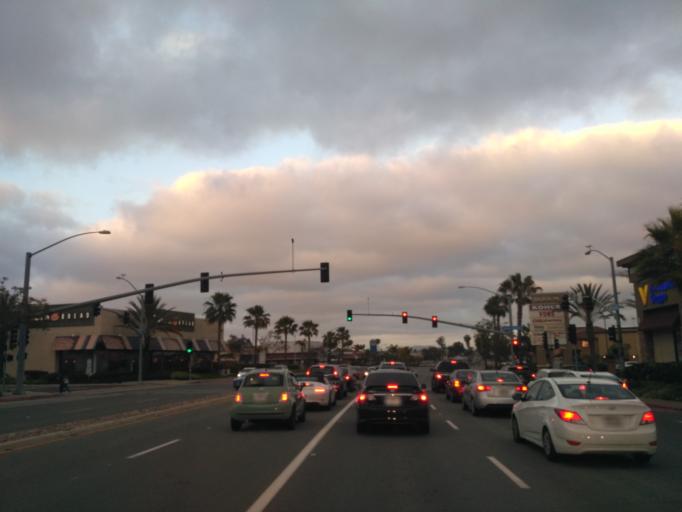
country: US
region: California
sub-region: San Diego County
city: La Jolla
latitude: 32.8198
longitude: -117.1806
